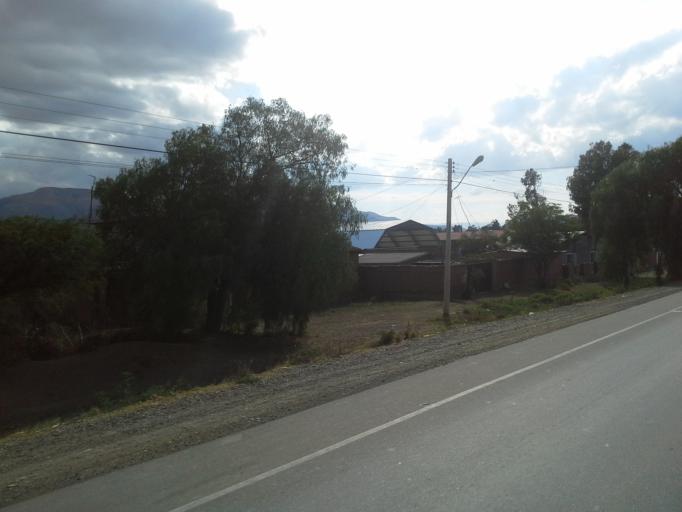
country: BO
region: Cochabamba
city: Tarata
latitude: -17.5423
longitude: -66.0328
